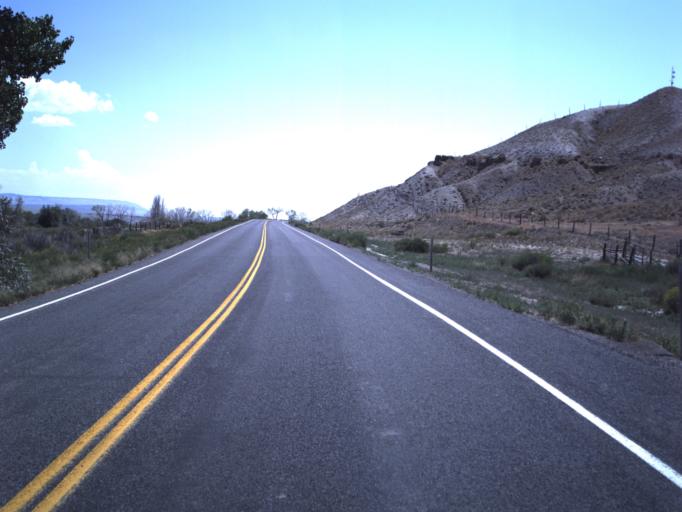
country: US
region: Utah
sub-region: Emery County
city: Orangeville
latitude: 39.2152
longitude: -111.0633
